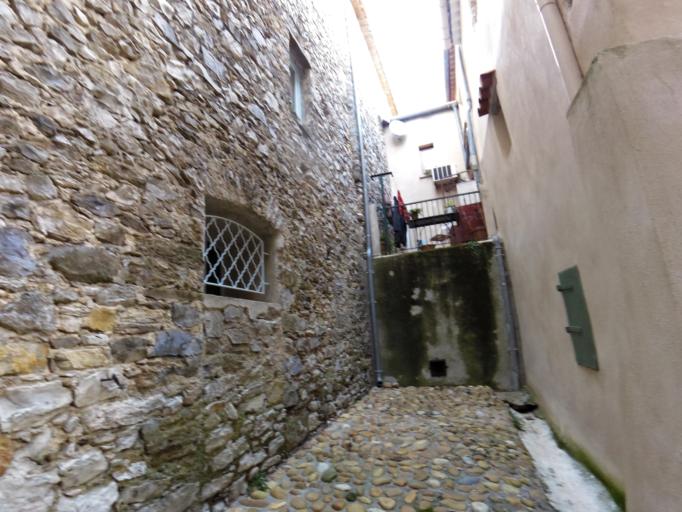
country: FR
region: Languedoc-Roussillon
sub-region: Departement du Gard
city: Sauve
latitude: 43.9901
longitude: 3.9550
